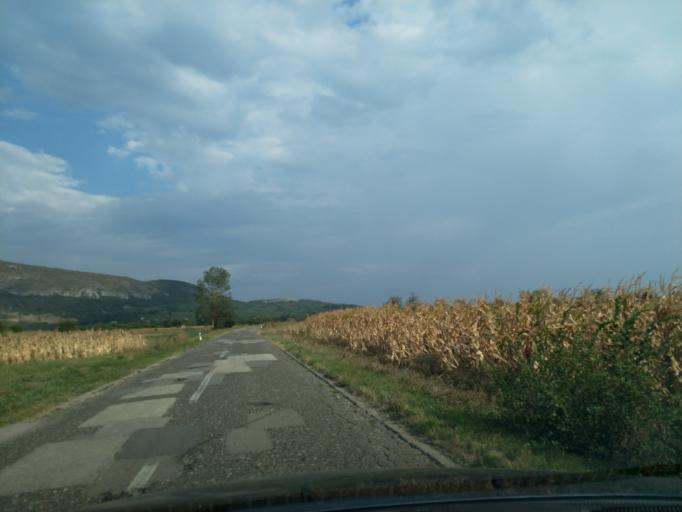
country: RS
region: Central Serbia
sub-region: Pomoravski Okrug
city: Paracin
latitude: 43.8244
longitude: 21.5293
